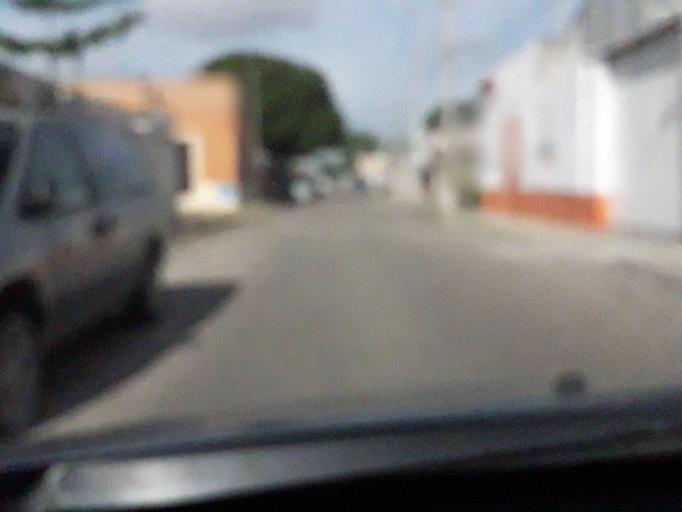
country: MX
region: Yucatan
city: Merida
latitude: 20.9558
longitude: -89.6161
